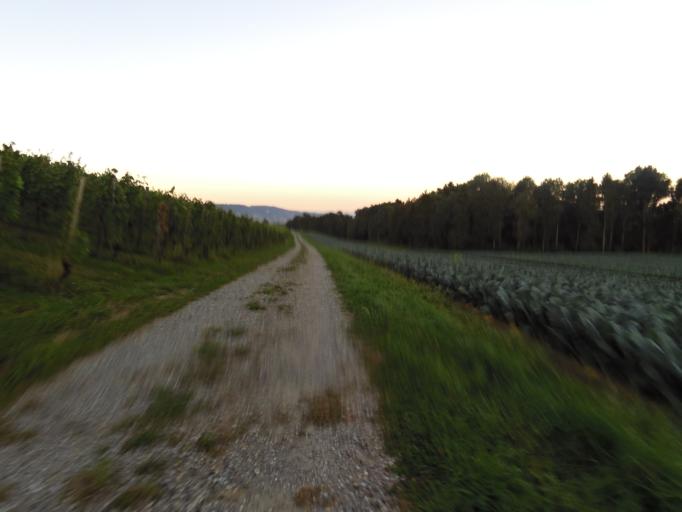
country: CH
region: Thurgau
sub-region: Weinfelden District
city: Wigoltingen
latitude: 47.5657
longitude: 9.0452
